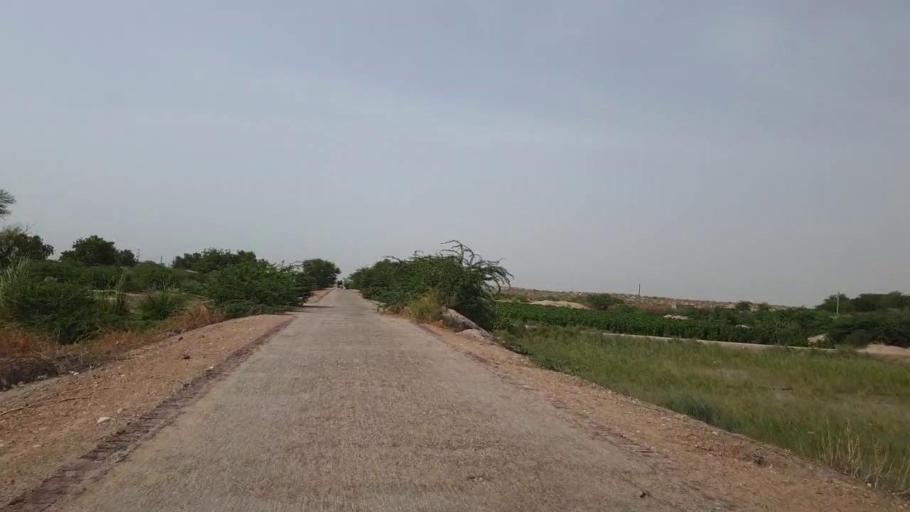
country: PK
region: Sindh
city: Bandhi
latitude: 26.5524
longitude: 68.3837
